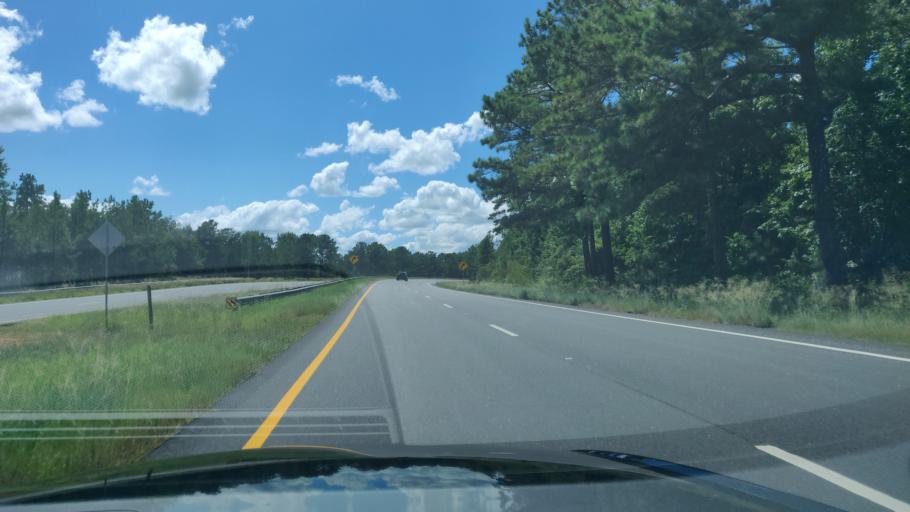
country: US
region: Georgia
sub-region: Stewart County
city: Richland
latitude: 32.1516
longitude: -84.6919
